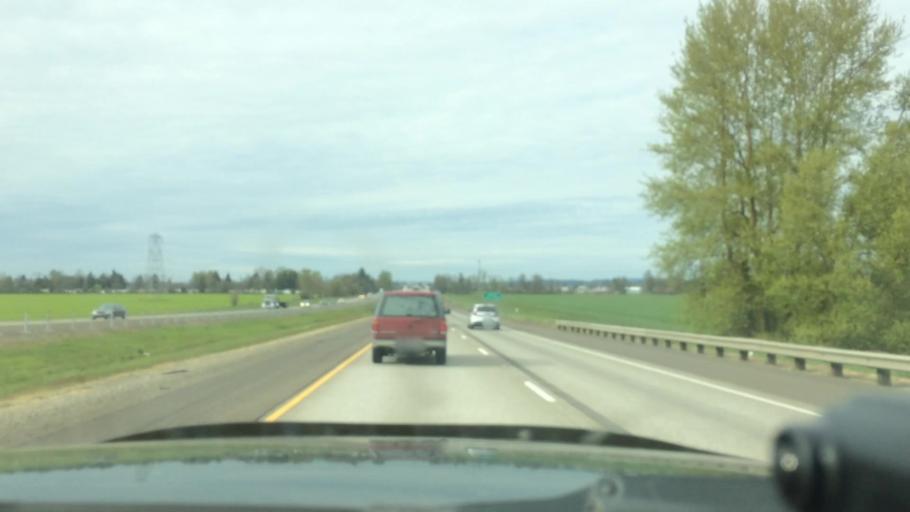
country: US
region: Oregon
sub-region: Linn County
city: Albany
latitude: 44.5988
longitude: -123.0618
